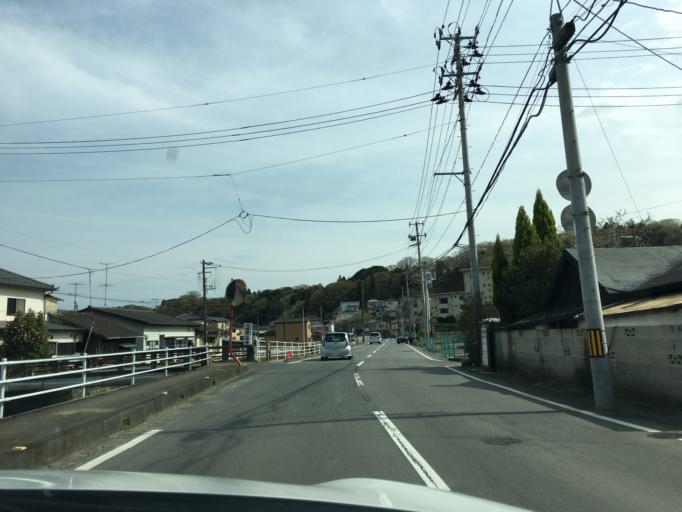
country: JP
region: Fukushima
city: Iwaki
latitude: 37.0414
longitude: 140.8445
